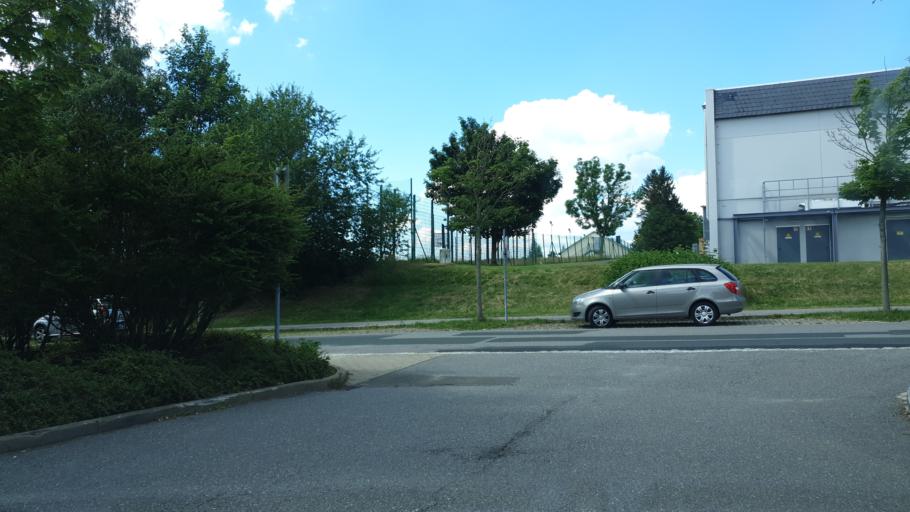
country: DE
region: Saxony
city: Marienberg
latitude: 50.6590
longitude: 13.1598
